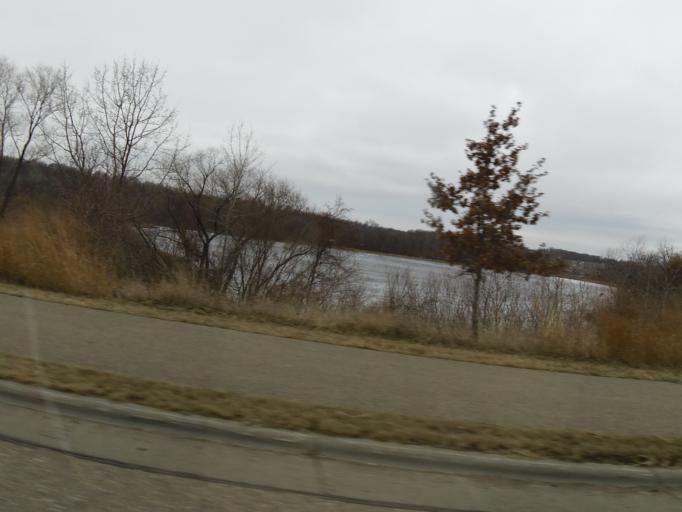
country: US
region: Minnesota
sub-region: Scott County
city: Prior Lake
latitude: 44.7389
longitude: -93.4398
